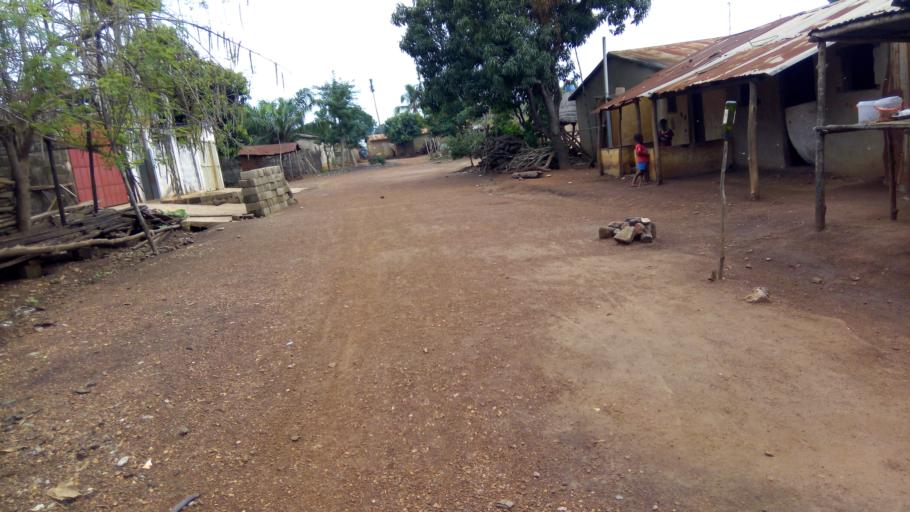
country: TG
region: Centrale
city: Sotouboua
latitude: 8.5652
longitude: 0.9809
